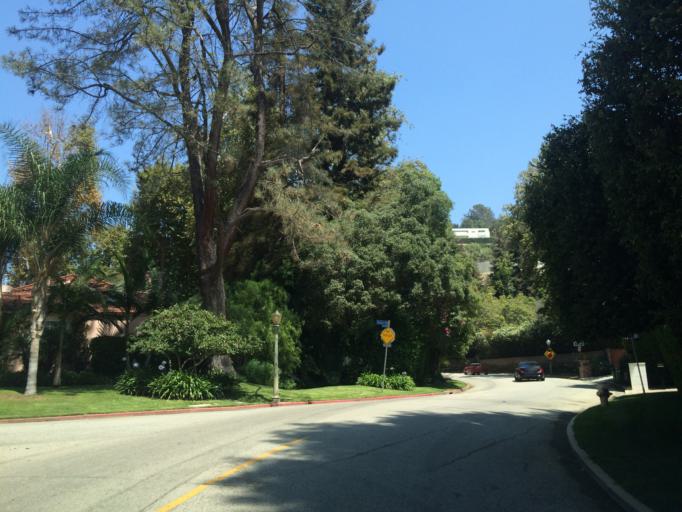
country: US
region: California
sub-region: Los Angeles County
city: Westwood, Los Angeles
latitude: 34.0851
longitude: -118.4451
